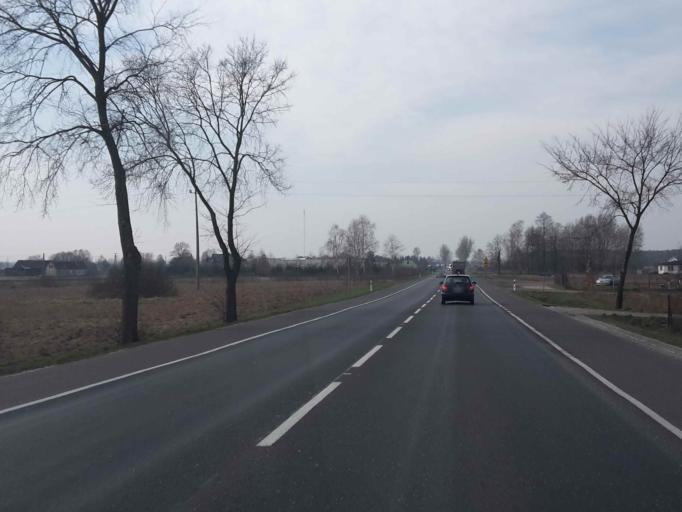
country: PL
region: Kujawsko-Pomorskie
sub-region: Powiat bydgoski
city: Biale Blota
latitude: 53.0757
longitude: 17.8405
